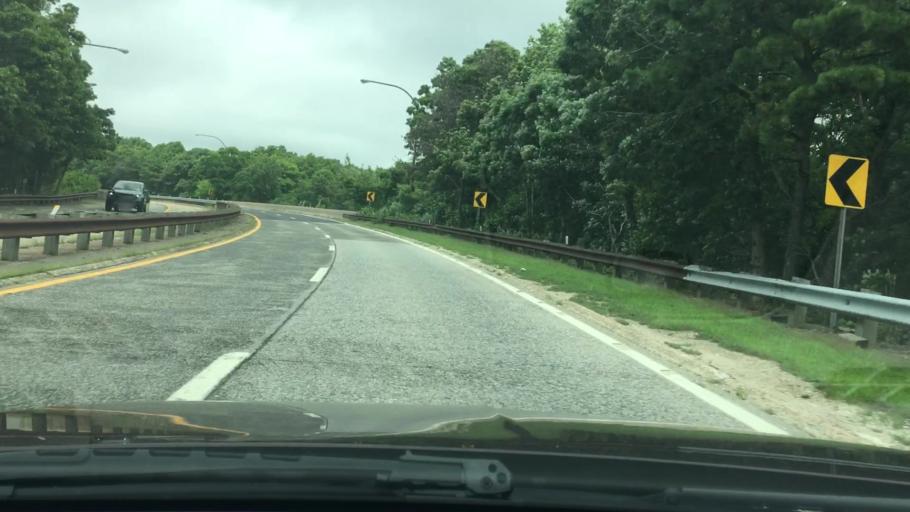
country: US
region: New York
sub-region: Suffolk County
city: Bay Wood
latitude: 40.7351
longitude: -73.2865
